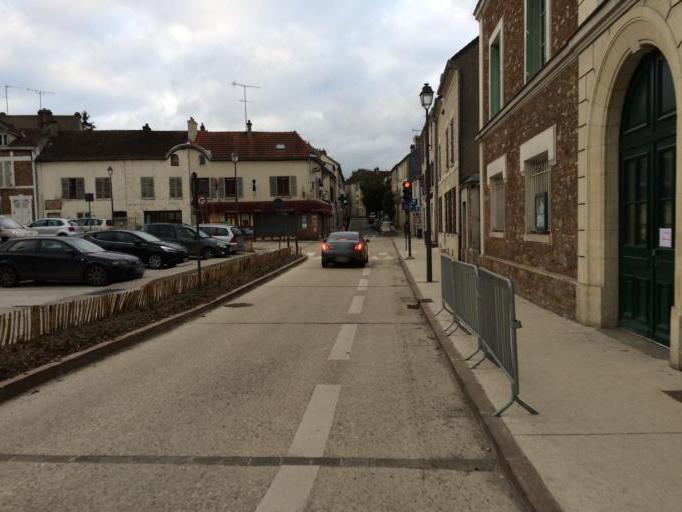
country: FR
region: Ile-de-France
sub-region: Departement de l'Essonne
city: Igny
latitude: 48.7424
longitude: 2.2263
